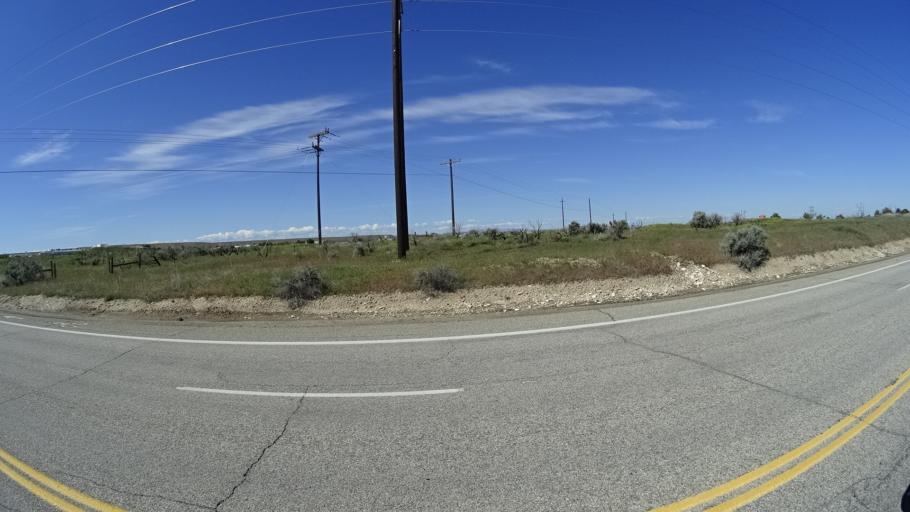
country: US
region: Idaho
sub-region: Ada County
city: Boise
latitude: 43.5386
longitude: -116.1466
